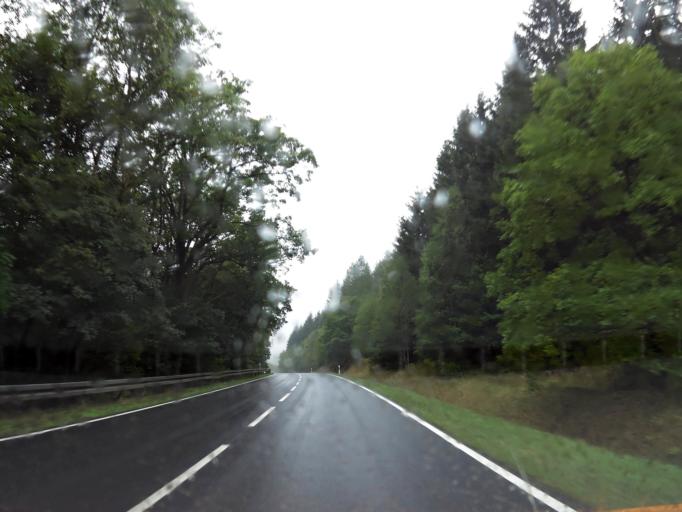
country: DE
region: Saxony-Anhalt
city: Friedrichsbrunn
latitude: 51.6512
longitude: 11.0193
